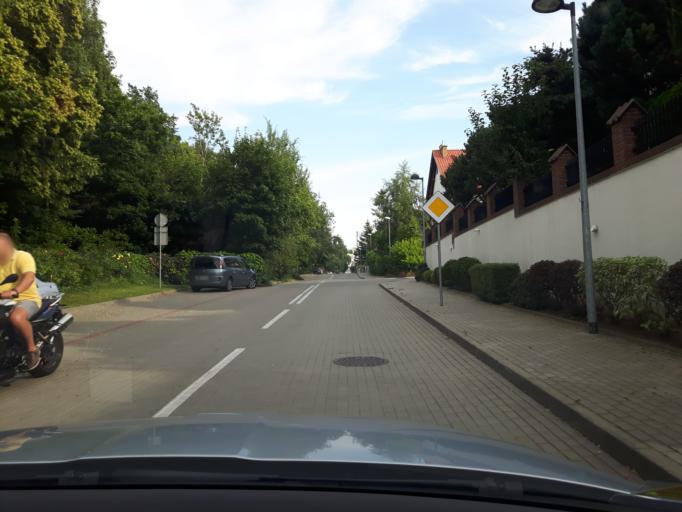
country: PL
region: Pomeranian Voivodeship
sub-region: Gdynia
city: Gdynia
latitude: 54.5028
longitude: 18.5470
